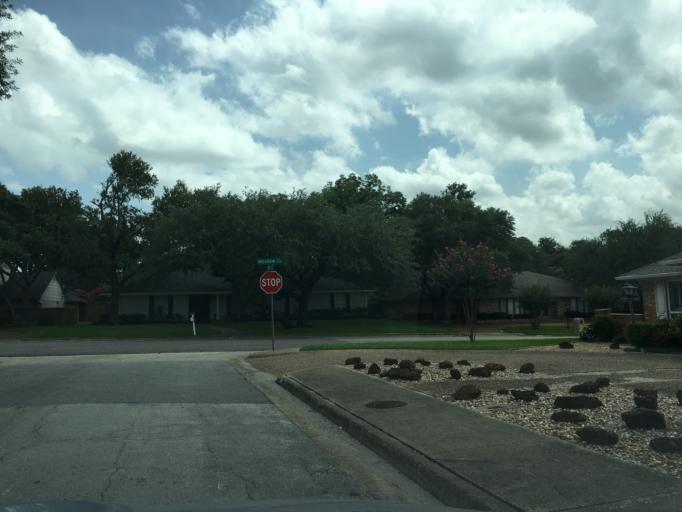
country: US
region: Texas
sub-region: Dallas County
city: University Park
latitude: 32.8879
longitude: -96.7797
